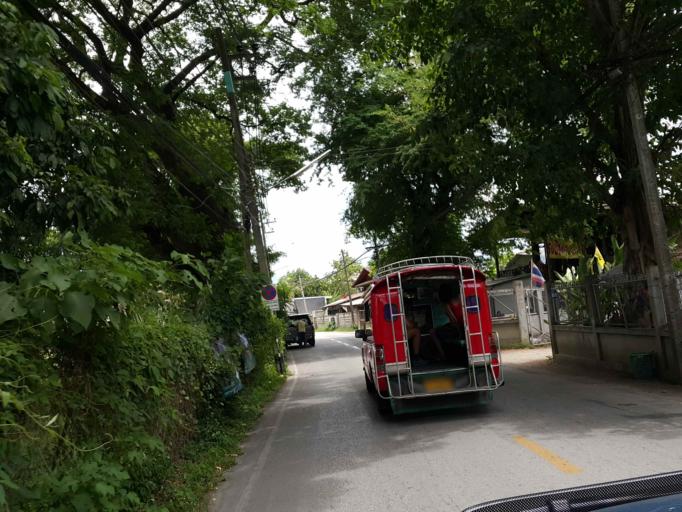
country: TH
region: Chiang Mai
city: Chiang Mai
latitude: 18.7744
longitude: 99.0100
